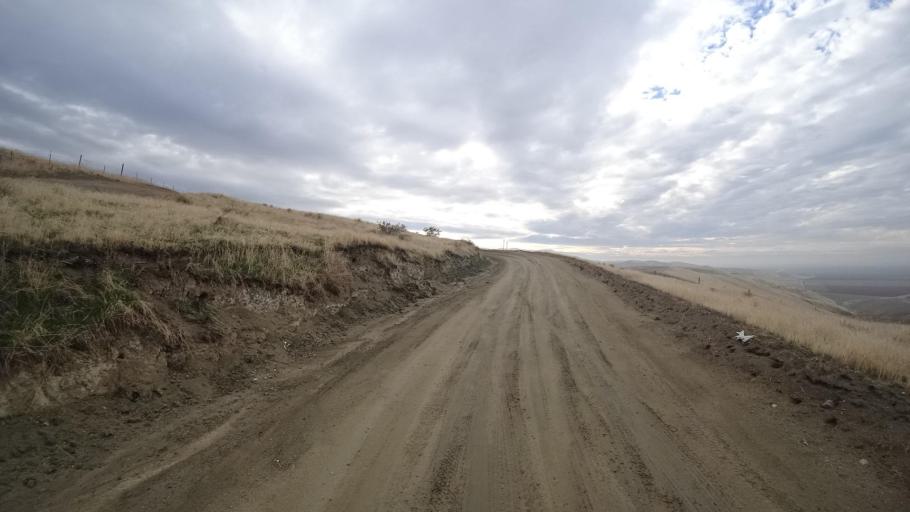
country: US
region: California
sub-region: Kern County
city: Arvin
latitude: 35.1403
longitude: -118.7953
